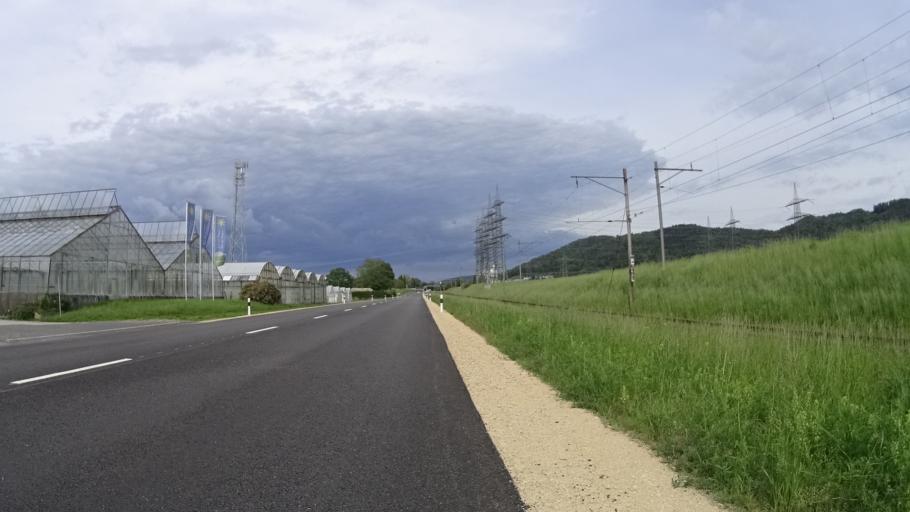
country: CH
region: Aargau
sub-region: Bezirk Laufenburg
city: Kaisten
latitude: 47.5516
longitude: 8.0410
